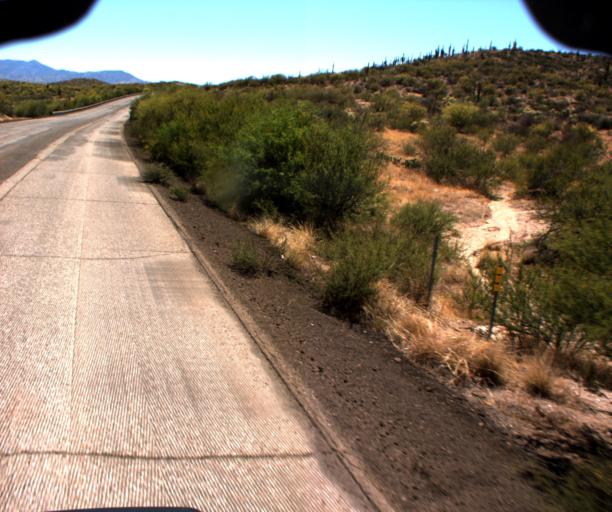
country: US
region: Arizona
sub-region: Pinal County
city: Mammoth
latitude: 32.6785
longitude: -110.6559
